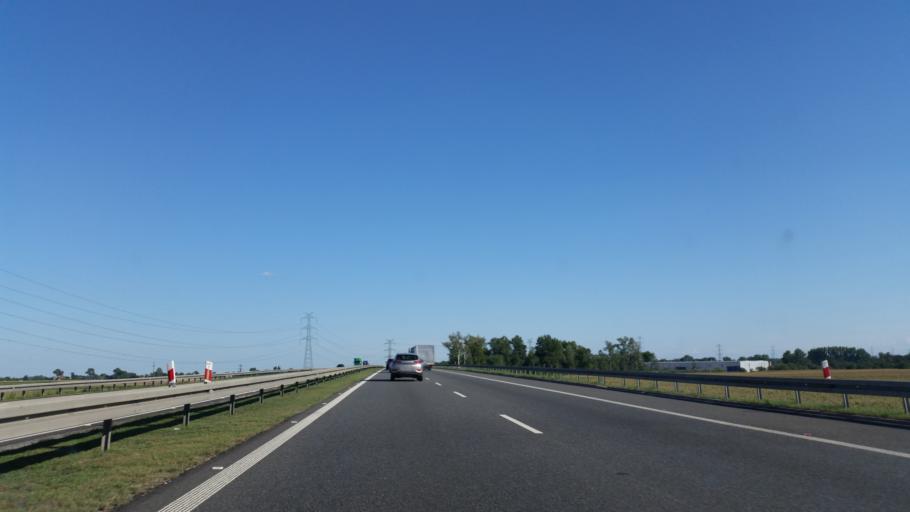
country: PL
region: Lower Silesian Voivodeship
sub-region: Powiat wroclawski
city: Zorawina
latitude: 50.9941
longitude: 17.0482
